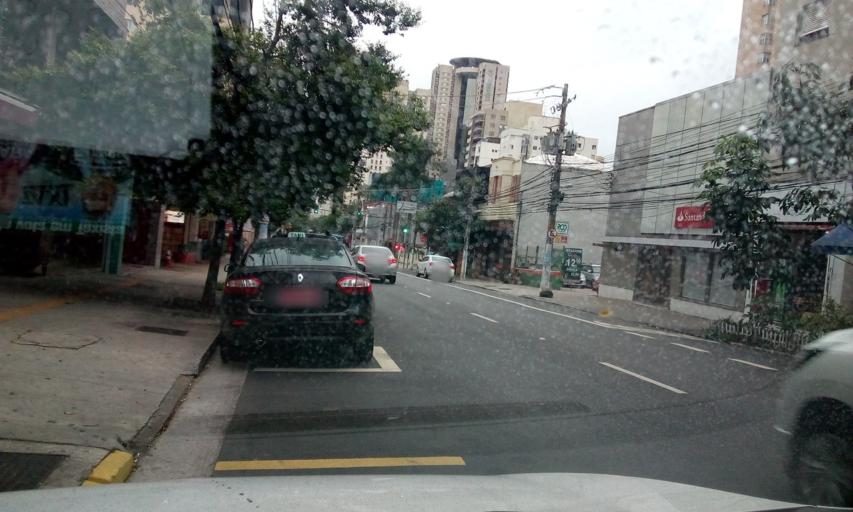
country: BR
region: Sao Paulo
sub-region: Sao Paulo
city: Sao Paulo
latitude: -23.5835
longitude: -46.6711
